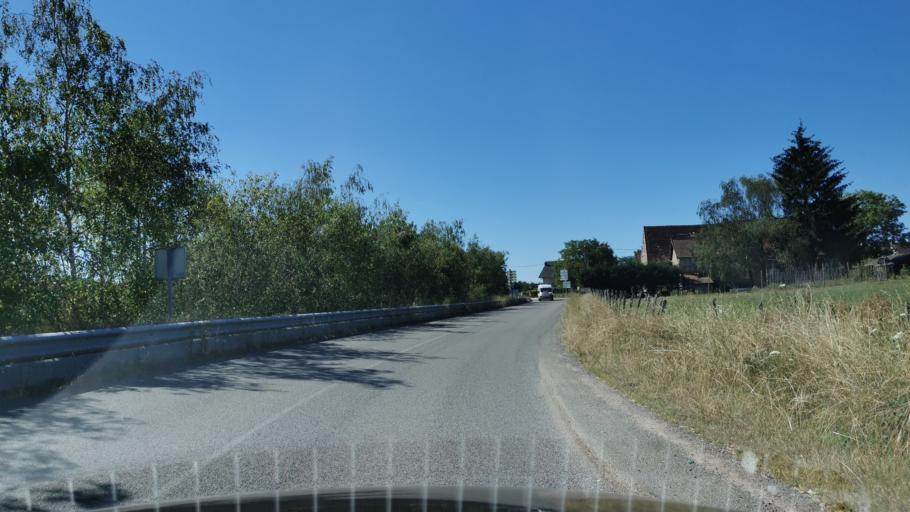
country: FR
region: Bourgogne
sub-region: Departement de Saone-et-Loire
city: Ecuisses
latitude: 46.7379
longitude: 4.5627
